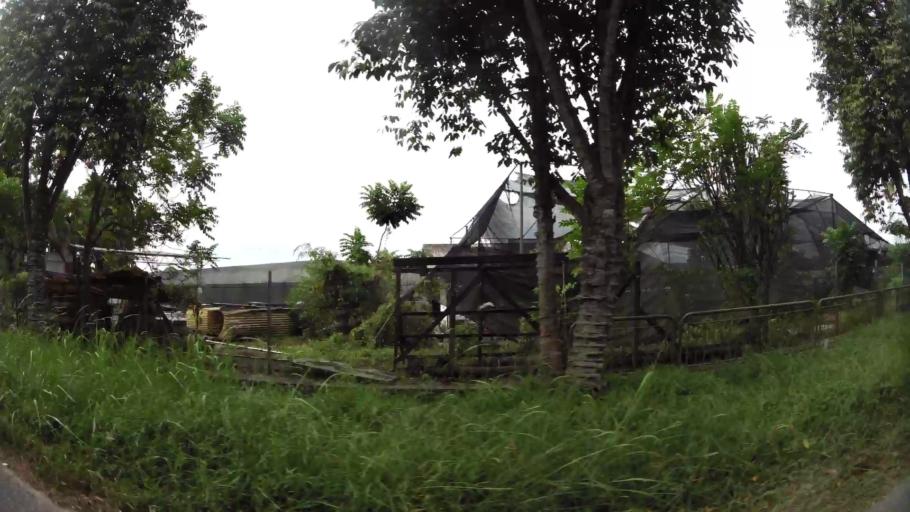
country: MY
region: Johor
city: Johor Bahru
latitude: 1.4424
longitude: 103.7113
